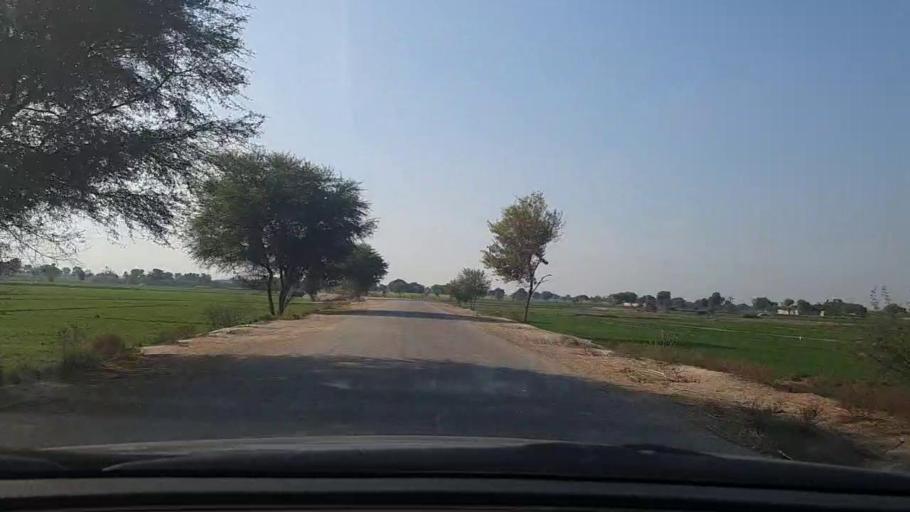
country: PK
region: Sindh
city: Daulatpur
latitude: 26.3189
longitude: 68.0522
